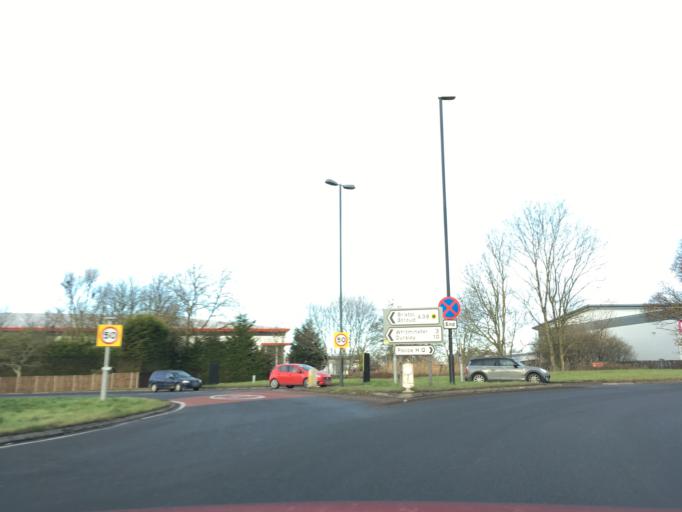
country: GB
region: England
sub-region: Gloucestershire
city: Stonehouse
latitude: 51.8055
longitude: -2.2901
